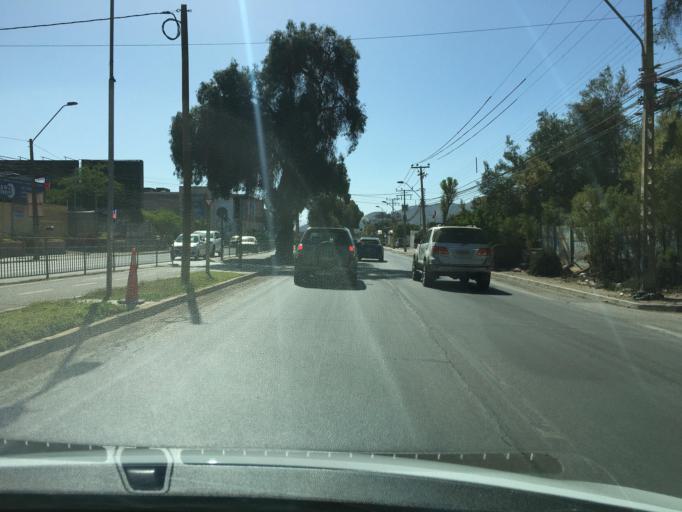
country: CL
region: Atacama
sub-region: Provincia de Copiapo
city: Copiapo
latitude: -27.3827
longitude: -70.3161
